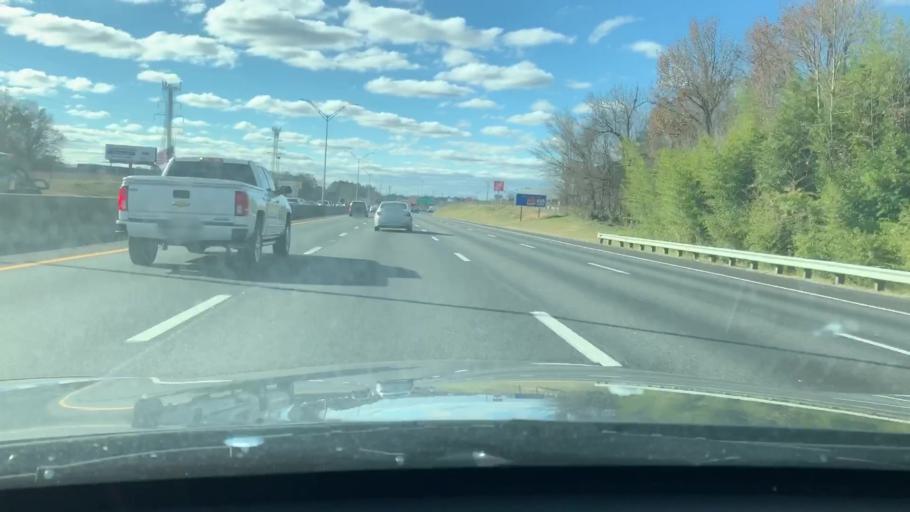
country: US
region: North Carolina
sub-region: Alamance County
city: Burlington
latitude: 36.0650
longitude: -79.4606
